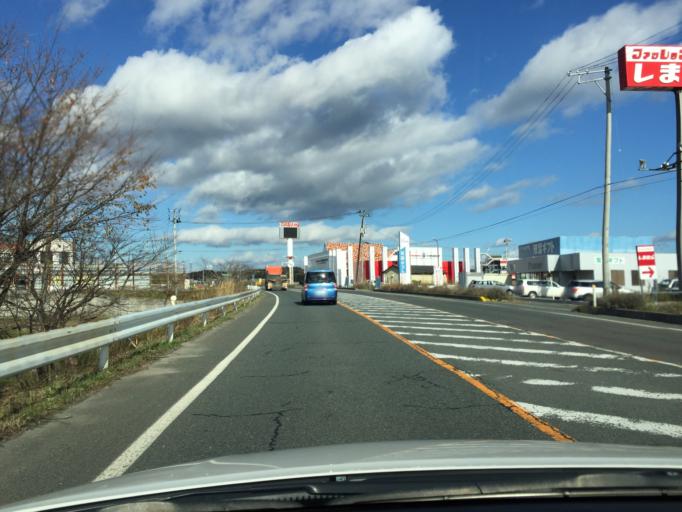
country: JP
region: Fukushima
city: Namie
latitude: 37.4878
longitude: 141.0054
